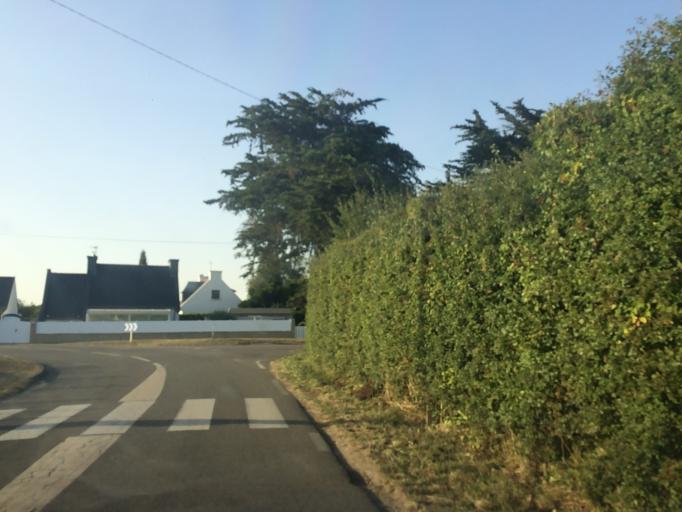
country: FR
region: Brittany
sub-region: Departement du Morbihan
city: Damgan
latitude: 47.5186
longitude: -2.5530
